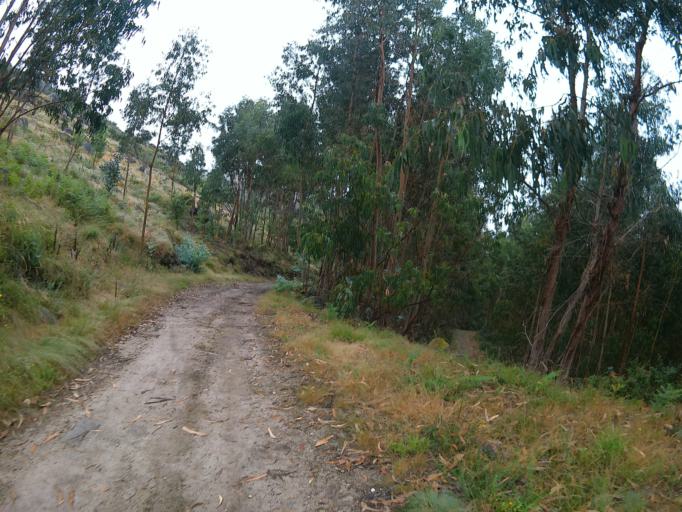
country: PT
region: Viana do Castelo
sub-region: Ponte de Lima
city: Ponte de Lima
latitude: 41.7281
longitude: -8.6075
